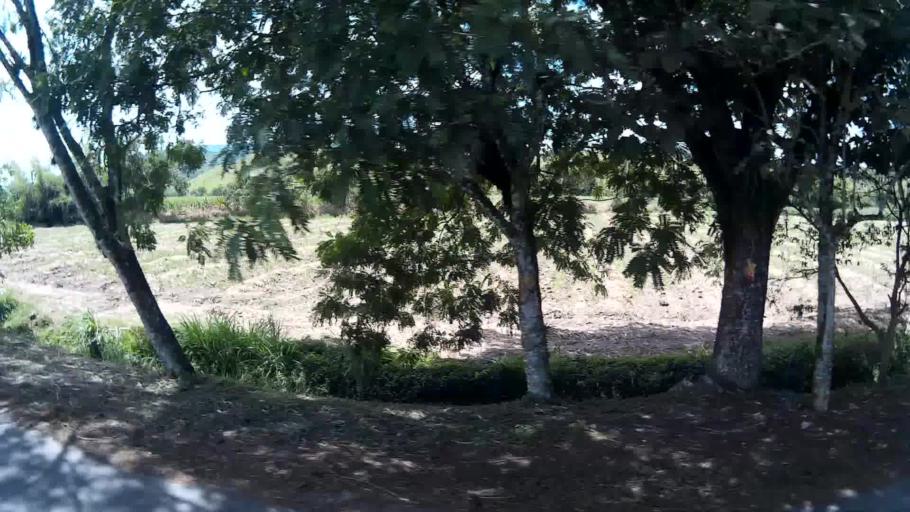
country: CO
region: Risaralda
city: La Virginia
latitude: 4.9064
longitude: -75.8698
